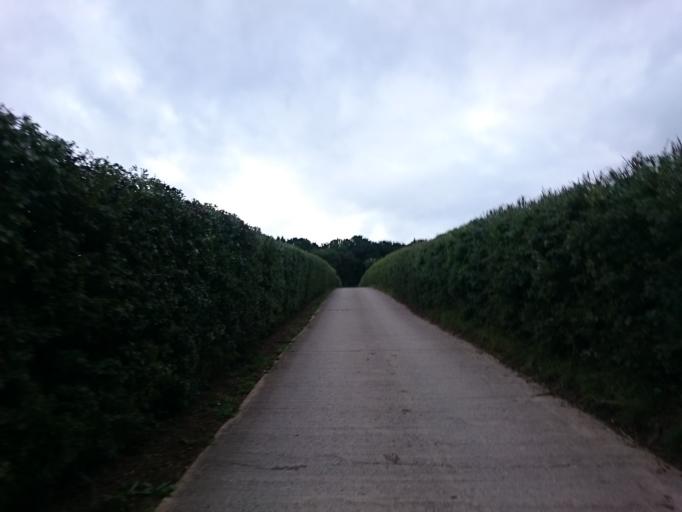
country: GB
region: England
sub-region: Oxfordshire
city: Boars Hill
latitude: 51.7210
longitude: -1.2757
